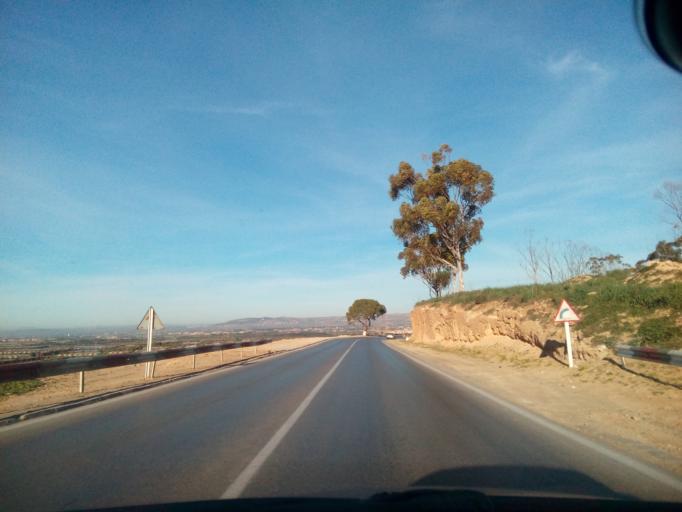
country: DZ
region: Mostaganem
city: Mostaganem
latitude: 35.7644
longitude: 0.2022
